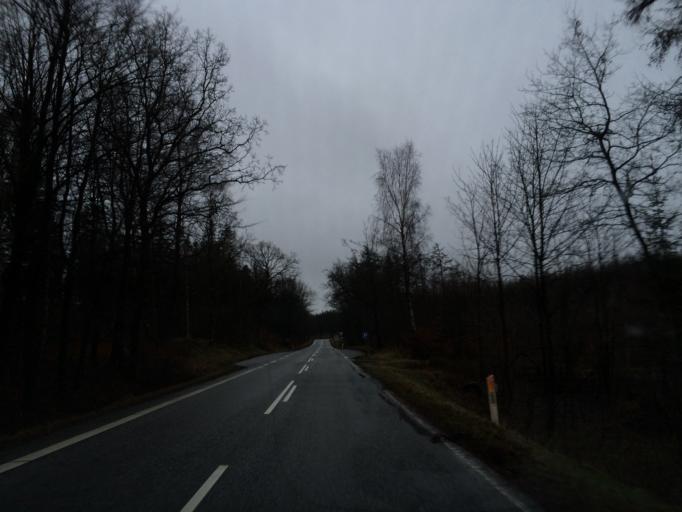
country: DK
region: North Denmark
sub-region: Rebild Kommune
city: Stovring
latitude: 56.8231
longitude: 9.8192
